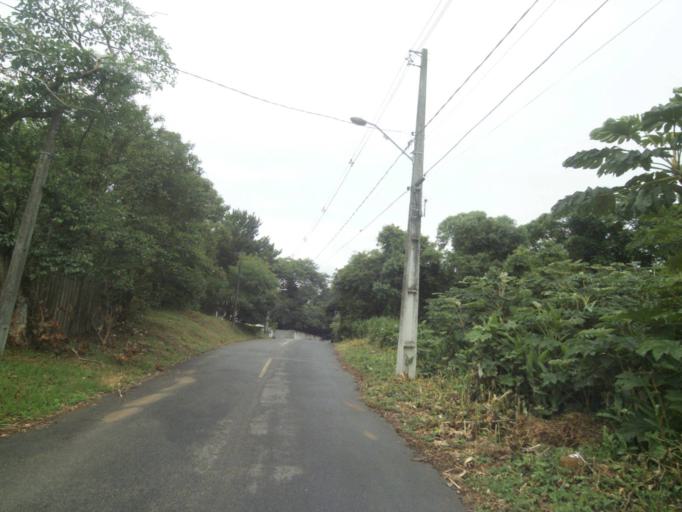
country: BR
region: Parana
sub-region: Curitiba
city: Curitiba
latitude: -25.4137
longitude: -49.2920
